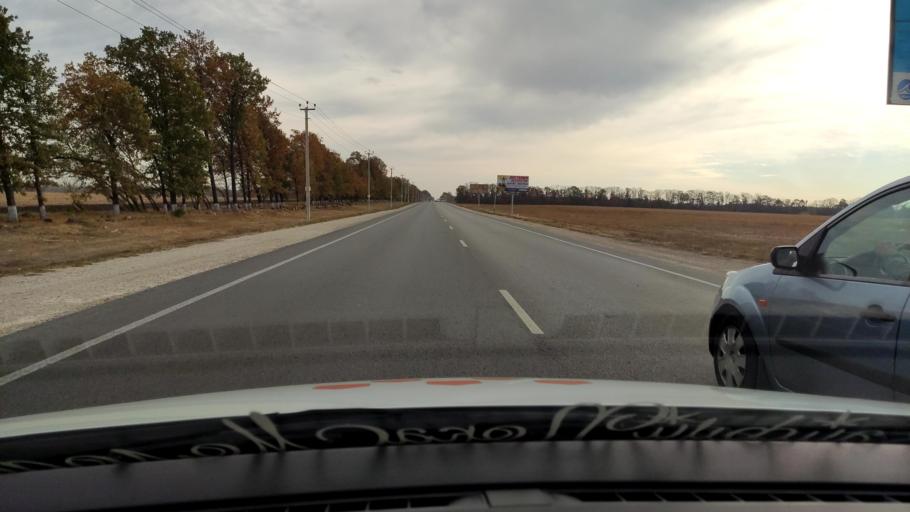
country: RU
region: Voronezj
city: Ramon'
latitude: 51.9287
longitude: 39.2338
